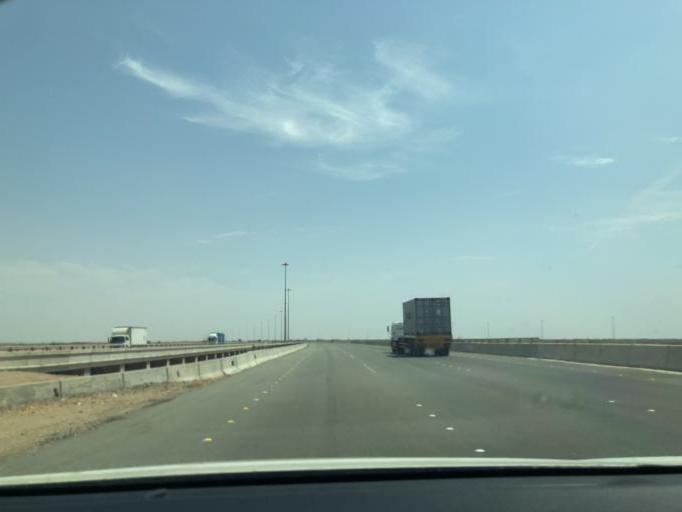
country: SA
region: Makkah
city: Rabigh
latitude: 22.2457
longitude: 39.1141
